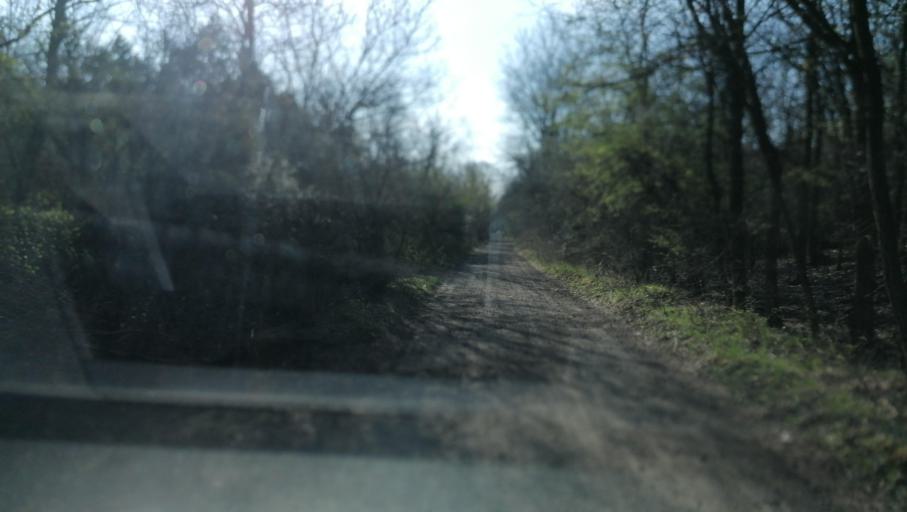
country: HU
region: Pest
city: Szentendre
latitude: 47.6682
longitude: 19.0919
